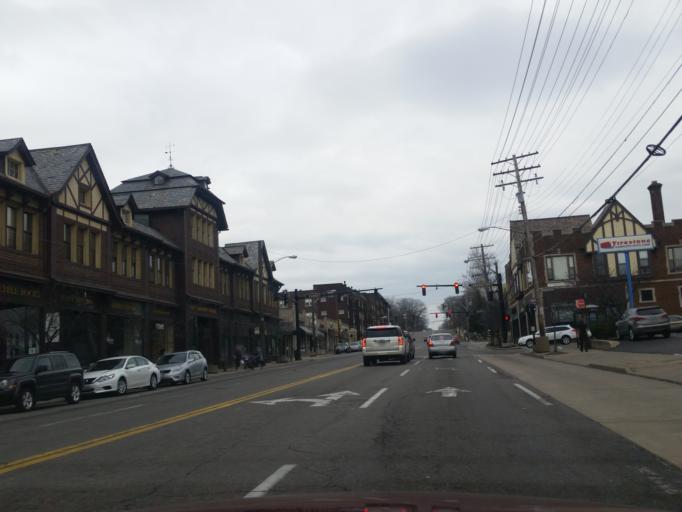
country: US
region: Ohio
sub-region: Cuyahoga County
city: East Cleveland
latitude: 41.5010
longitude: -81.5941
